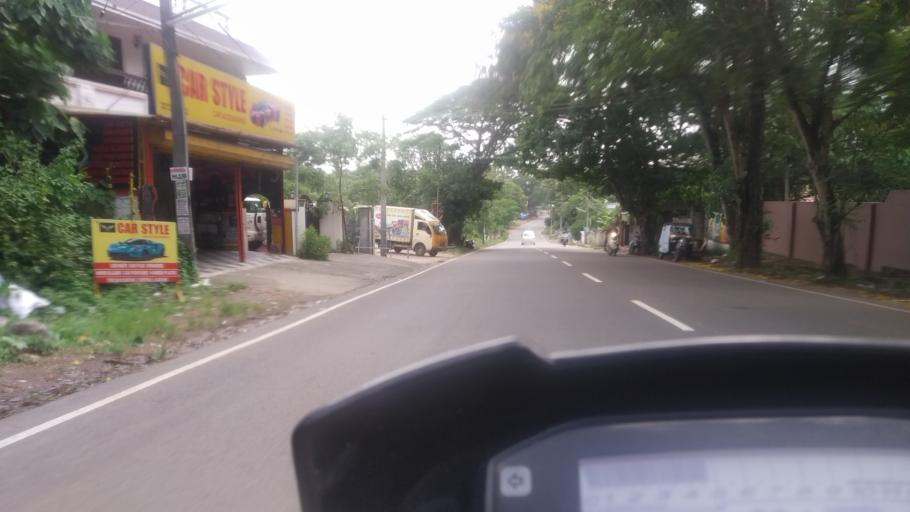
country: IN
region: Kerala
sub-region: Ernakulam
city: Aluva
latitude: 10.1264
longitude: 76.3238
